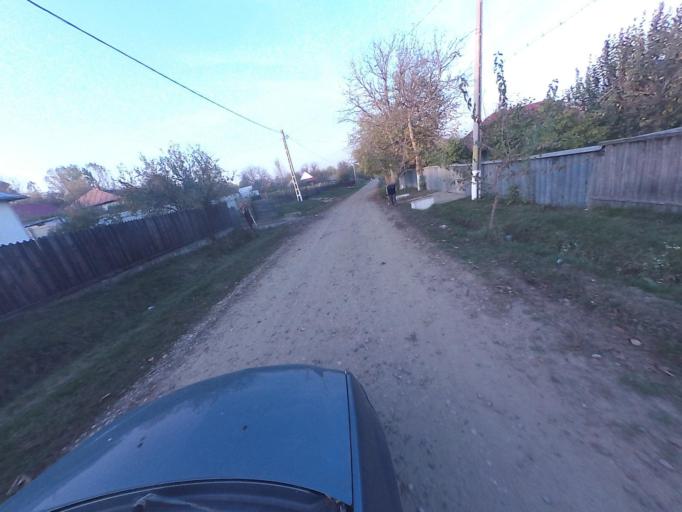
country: RO
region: Vaslui
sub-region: Comuna Bacesti
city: Bacesti
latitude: 46.8018
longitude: 27.2243
